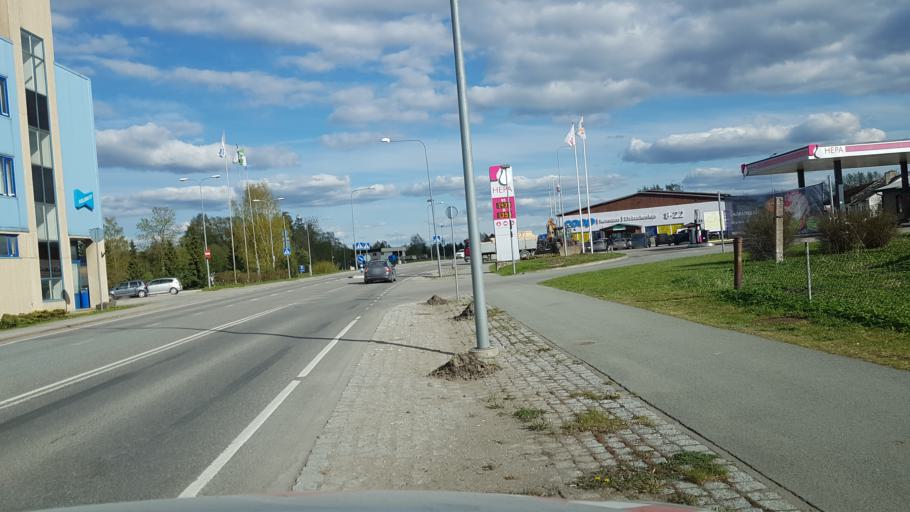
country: EE
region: Raplamaa
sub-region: Rapla vald
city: Rapla
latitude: 59.0112
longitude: 24.8055
